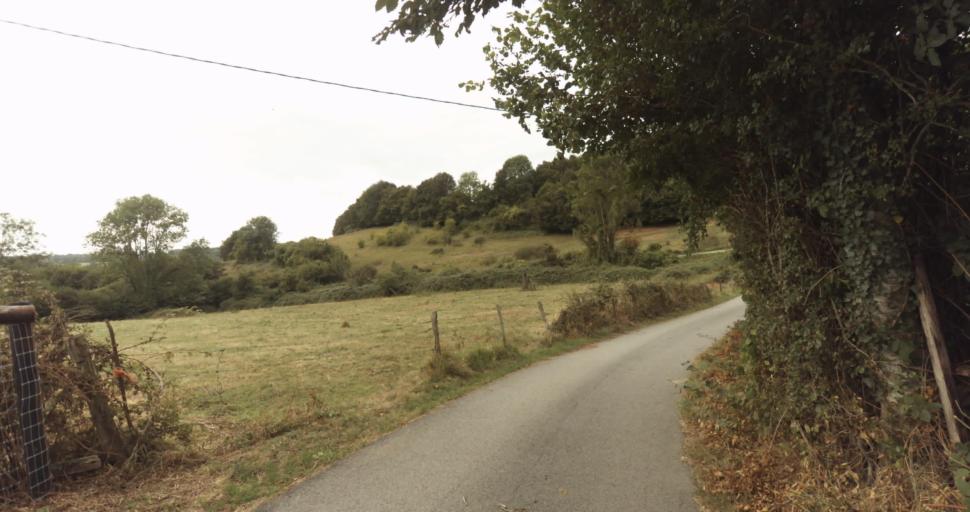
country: FR
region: Lower Normandy
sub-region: Departement de l'Orne
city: Gace
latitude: 48.8288
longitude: 0.2945
